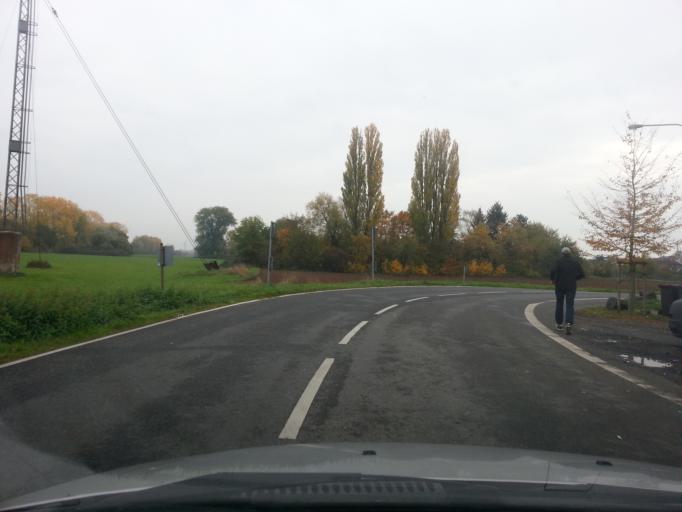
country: DE
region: Hesse
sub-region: Regierungsbezirk Darmstadt
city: Muehlheim am Main
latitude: 50.1291
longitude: 8.8370
